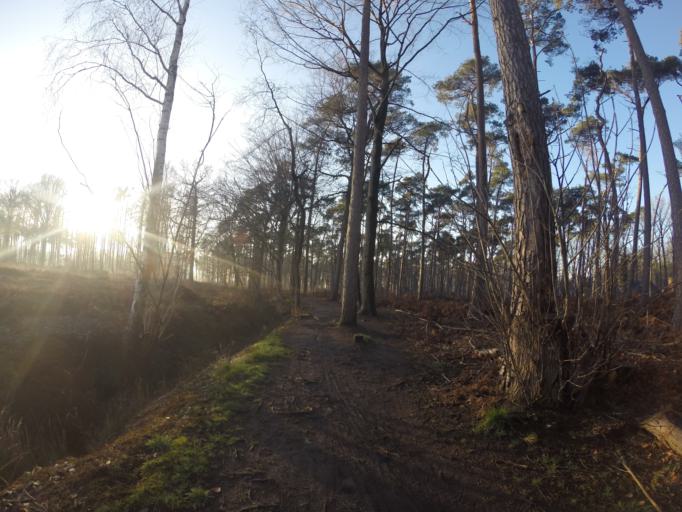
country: BE
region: Flanders
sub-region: Provincie West-Vlaanderen
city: Wingene
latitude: 51.0949
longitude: 3.2968
